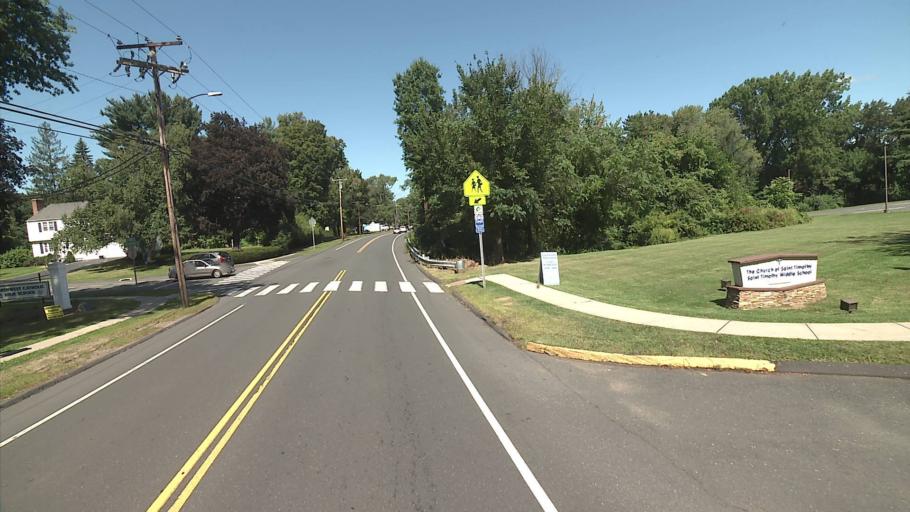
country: US
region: Connecticut
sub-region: Hartford County
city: West Hartford
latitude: 41.8005
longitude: -72.7496
